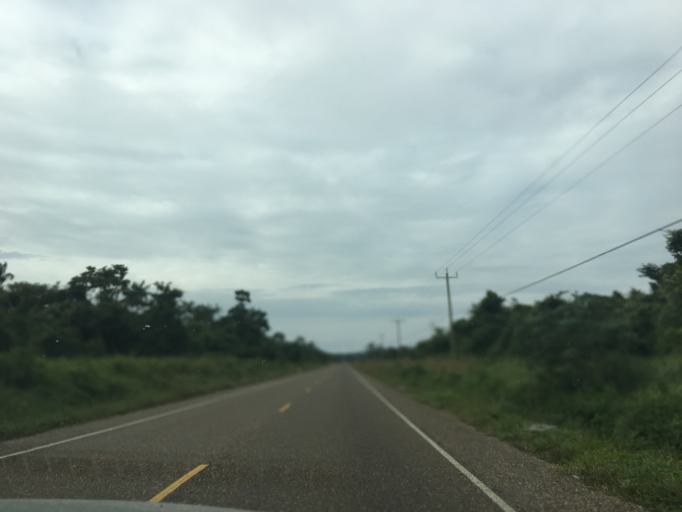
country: BZ
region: Stann Creek
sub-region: Dangriga
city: Dangriga
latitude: 16.8573
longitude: -88.3060
